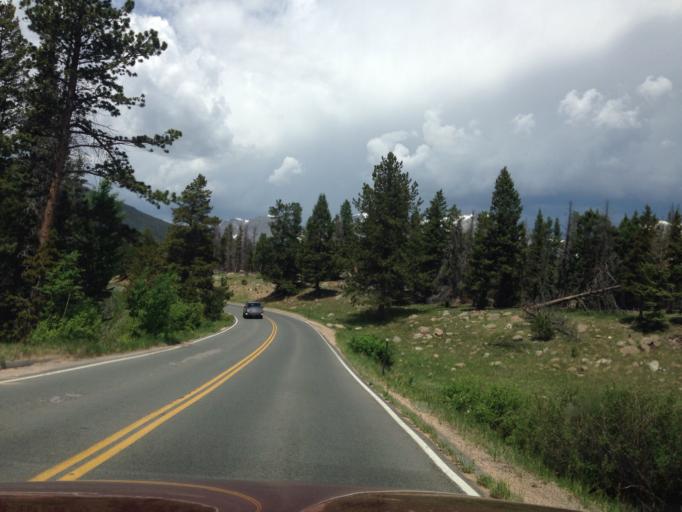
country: US
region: Colorado
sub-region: Larimer County
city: Estes Park
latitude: 40.3922
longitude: -105.6230
